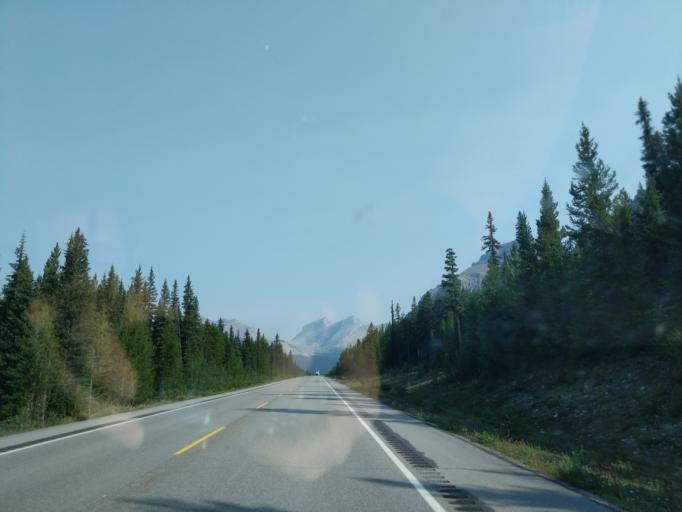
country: CA
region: Alberta
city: Lake Louise
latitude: 51.6063
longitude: -116.3116
